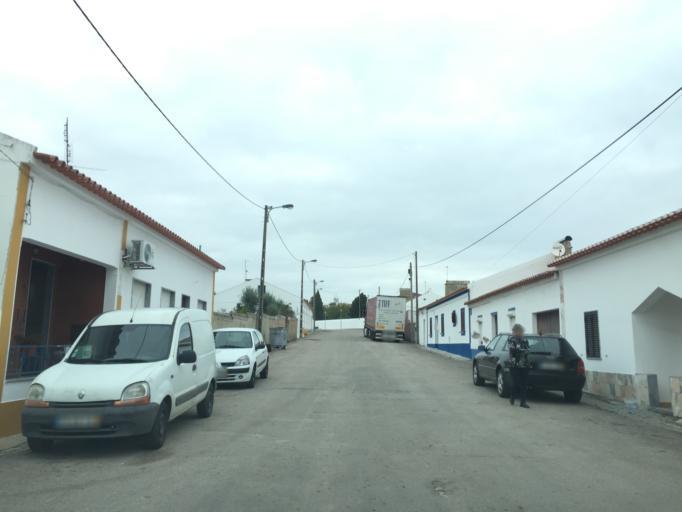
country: PT
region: Portalegre
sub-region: Fronteira
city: Vale da Amoreira
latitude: 39.0457
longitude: -7.7632
